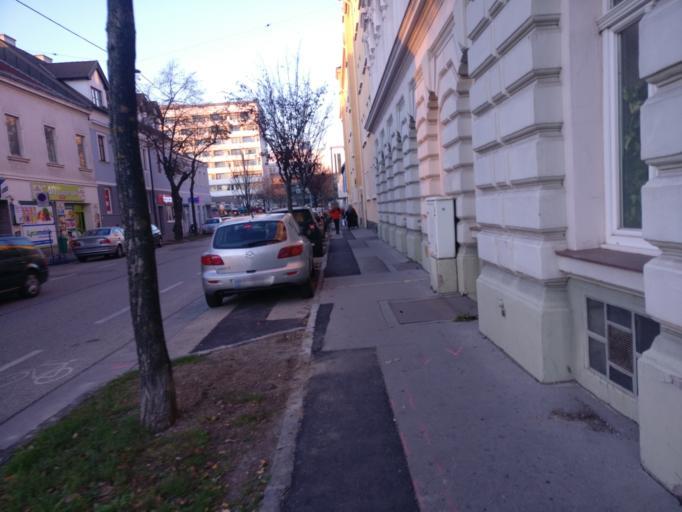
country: AT
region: Lower Austria
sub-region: Sankt Polten Stadt
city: Sankt Poelten
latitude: 48.2118
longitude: 15.6251
